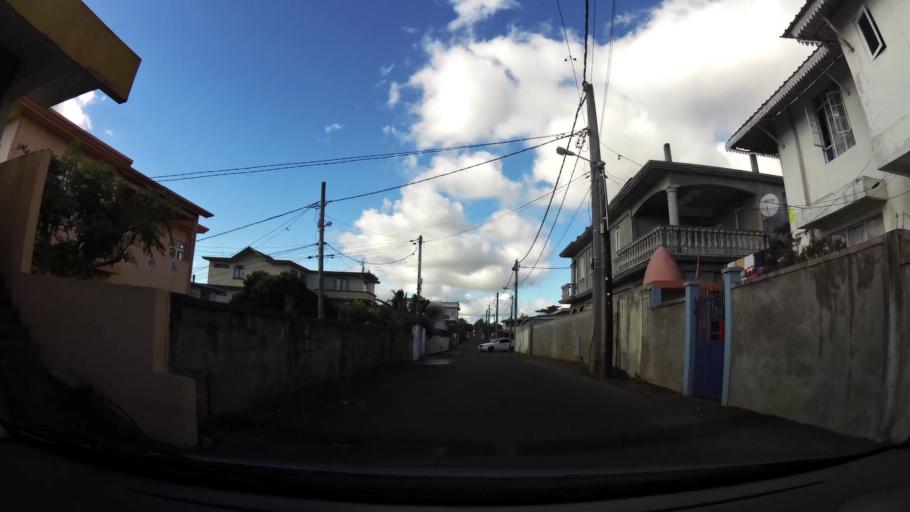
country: MU
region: Plaines Wilhems
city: Vacoas
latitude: -20.2929
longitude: 57.4852
